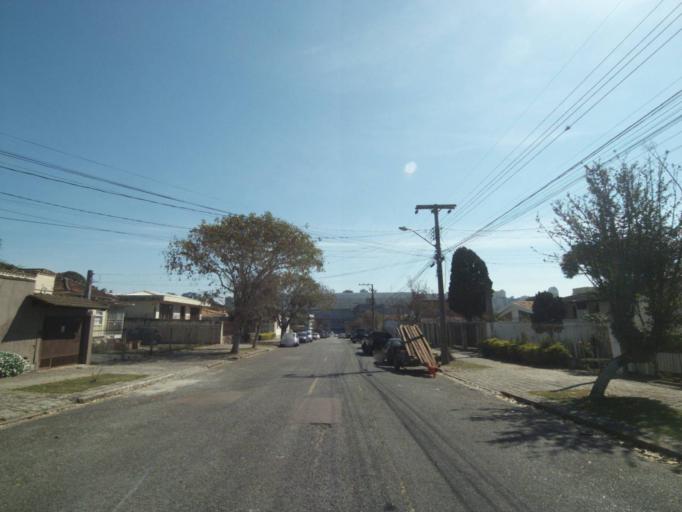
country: BR
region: Parana
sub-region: Curitiba
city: Curitiba
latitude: -25.4521
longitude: -49.2755
